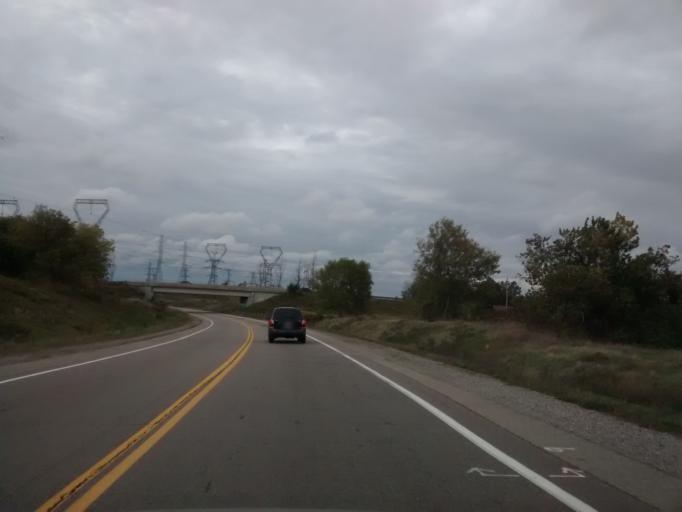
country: CA
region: Ontario
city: Ancaster
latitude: 43.0614
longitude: -79.9813
